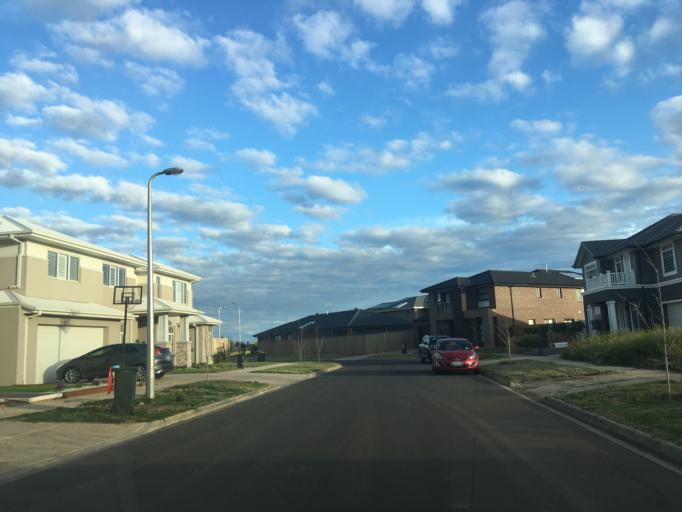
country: AU
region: Victoria
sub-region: Wyndham
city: Hoppers Crossing
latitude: -37.8867
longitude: 144.7135
